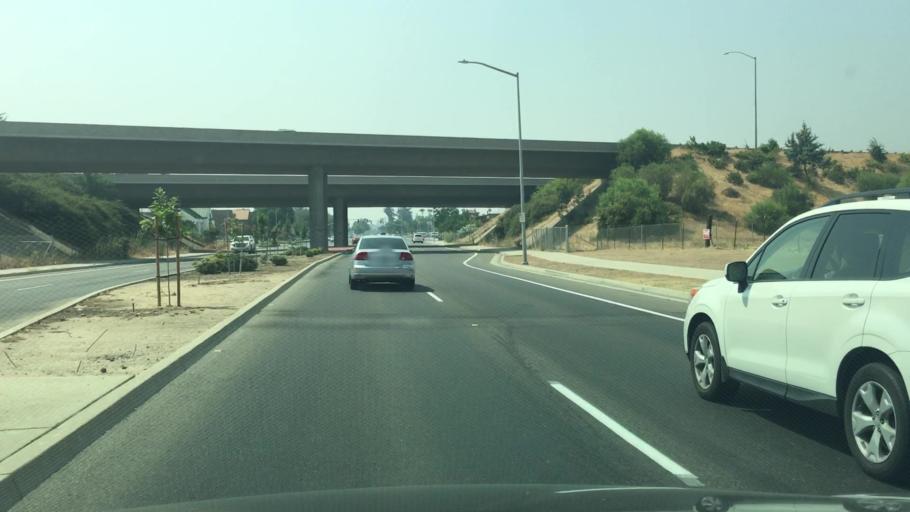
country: US
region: California
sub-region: Fresno County
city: Clovis
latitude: 36.8407
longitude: -119.7000
